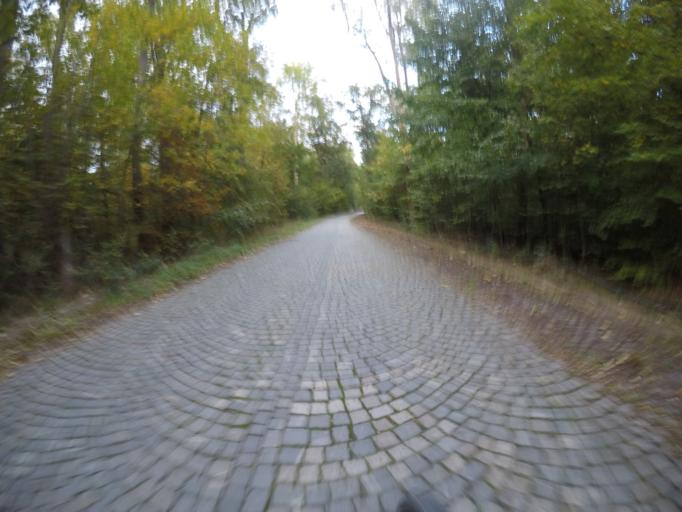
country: DE
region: Baden-Wuerttemberg
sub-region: Regierungsbezirk Stuttgart
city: Schonaich
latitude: 48.6981
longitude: 9.0670
